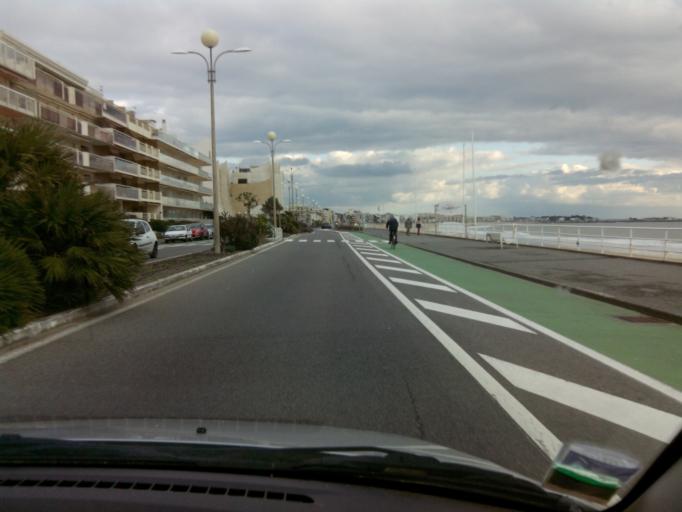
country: FR
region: Pays de la Loire
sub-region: Departement de la Loire-Atlantique
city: La Baule-Escoublac
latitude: 47.2751
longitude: -2.3625
